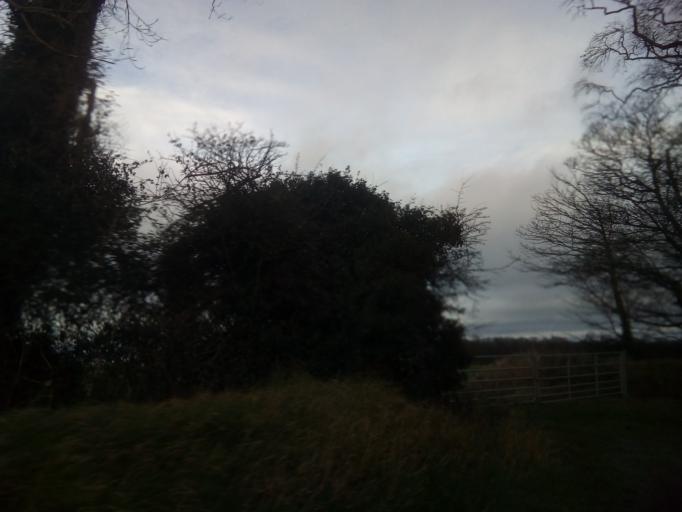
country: IE
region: Leinster
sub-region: Fingal County
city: Skerries
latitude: 53.5662
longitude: -6.1388
